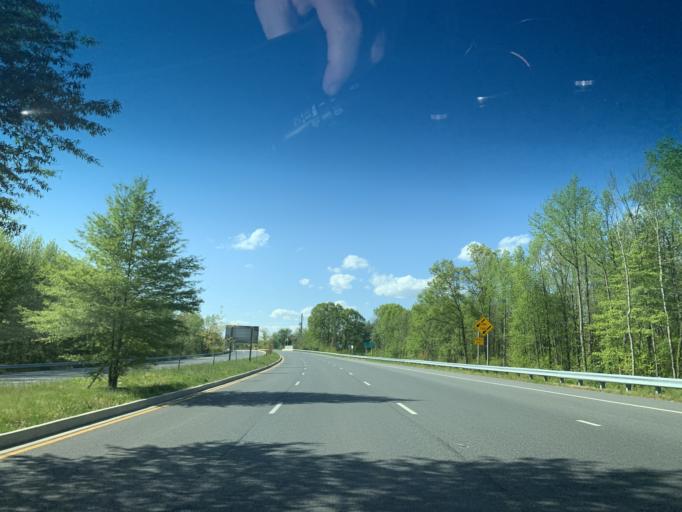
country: US
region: Maryland
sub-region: Harford County
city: Aberdeen
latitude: 39.5127
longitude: -76.1564
